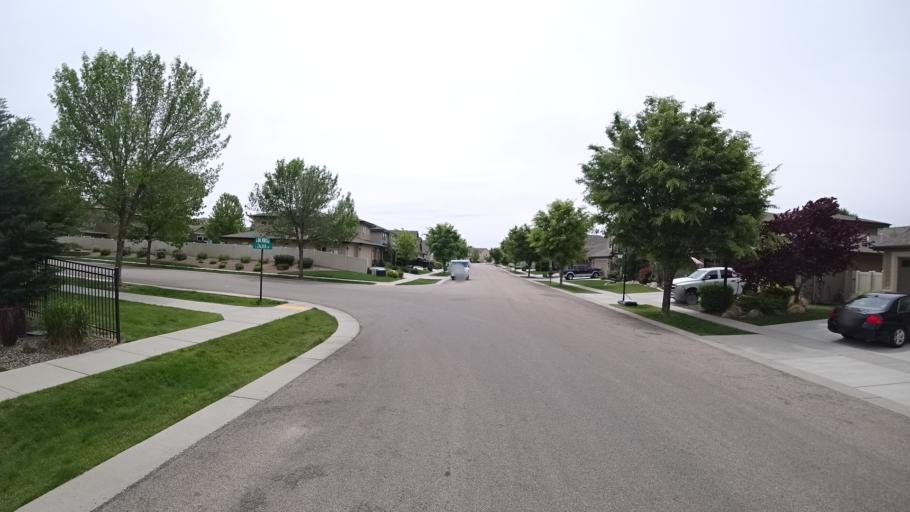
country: US
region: Idaho
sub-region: Ada County
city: Meridian
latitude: 43.5663
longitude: -116.3643
